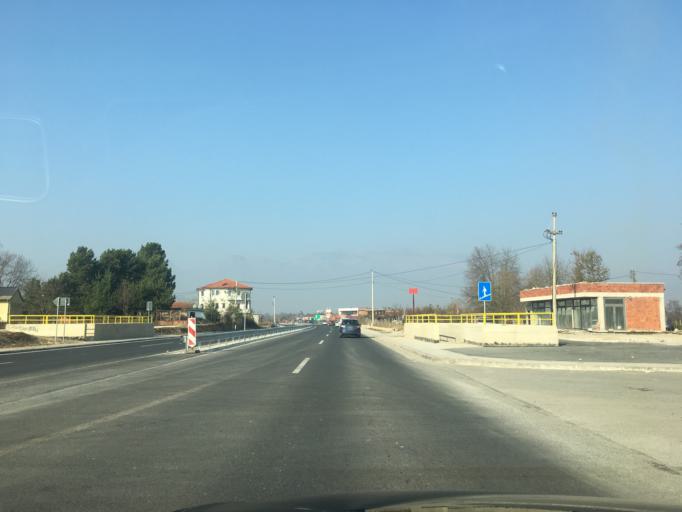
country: XK
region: Pec
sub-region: Komuna e Pejes
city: Dubova (Driloni)
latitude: 42.6561
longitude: 20.3889
